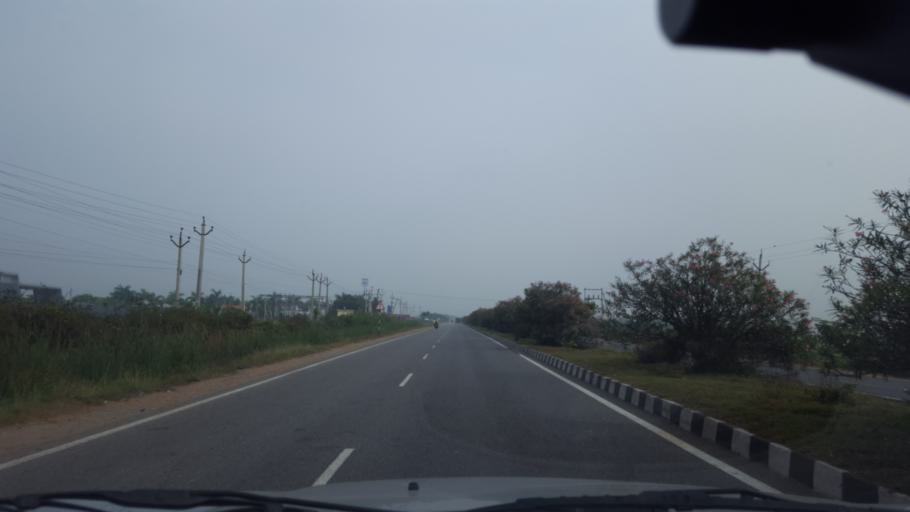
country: IN
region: Andhra Pradesh
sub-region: Guntur
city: Chilakalurupet
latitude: 16.0624
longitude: 80.1494
